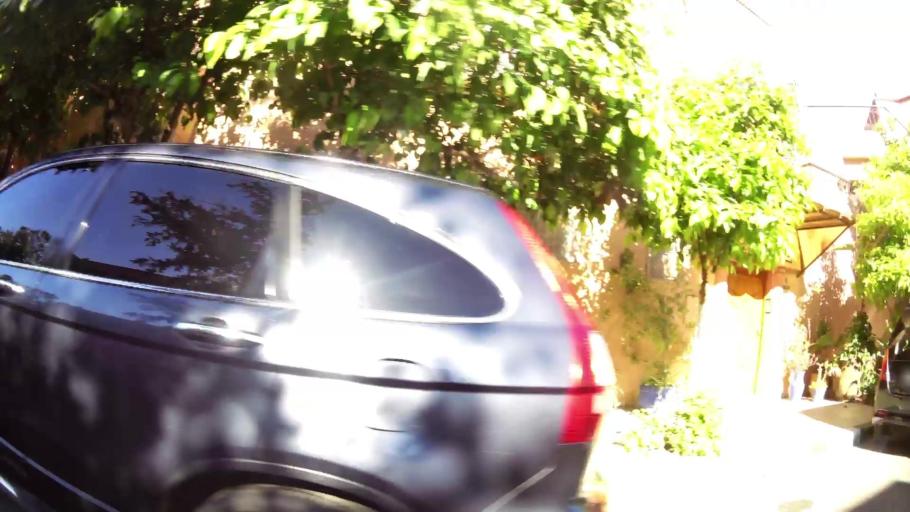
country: MA
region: Marrakech-Tensift-Al Haouz
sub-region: Marrakech
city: Marrakesh
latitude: 31.6451
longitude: -8.0168
